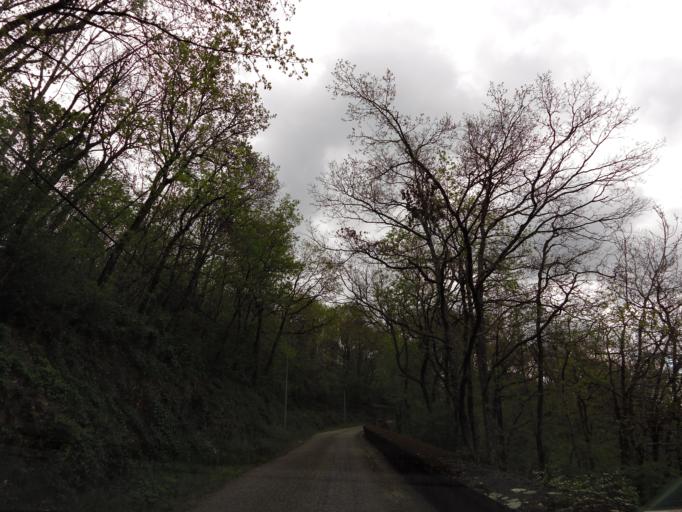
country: FR
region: Languedoc-Roussillon
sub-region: Departement de l'Aude
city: Saint-Martin-Lalande
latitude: 43.3698
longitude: 2.0613
